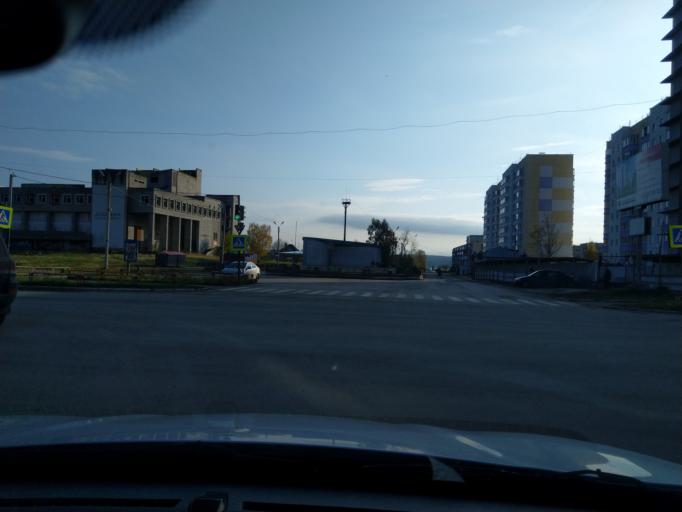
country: RU
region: Perm
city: Dobryanka
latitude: 58.4630
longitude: 56.4000
